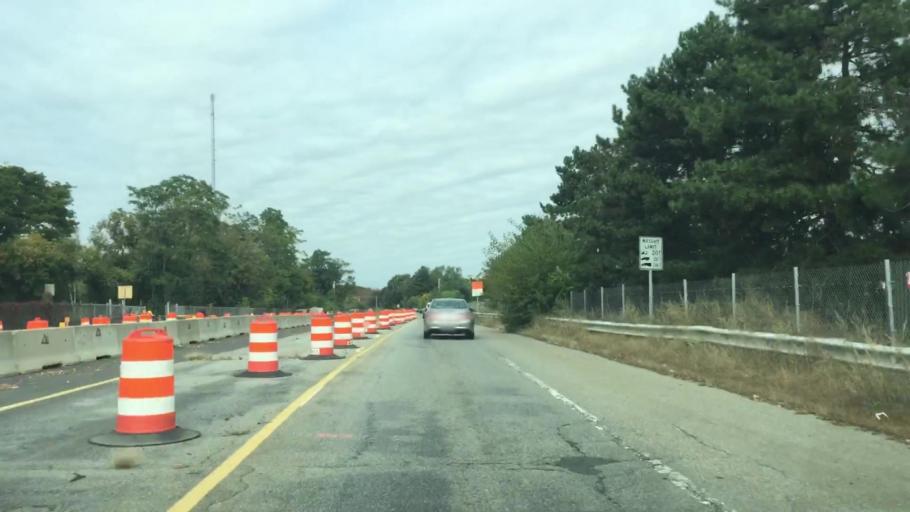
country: US
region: Massachusetts
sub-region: Middlesex County
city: Dracut
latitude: 42.6566
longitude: -71.3146
